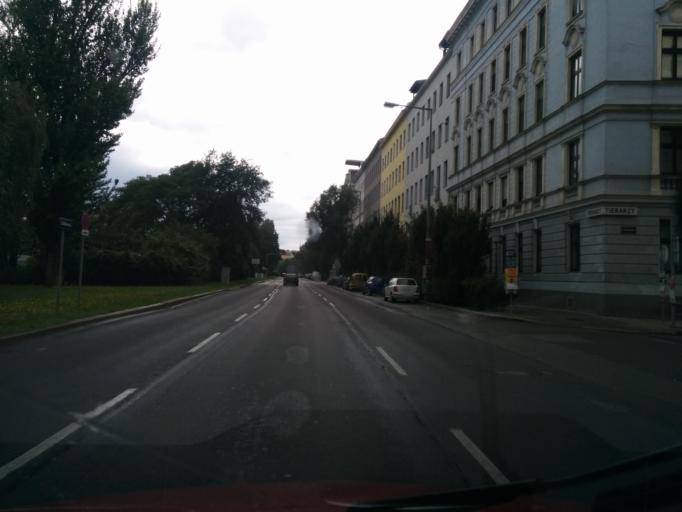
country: AT
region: Vienna
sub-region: Wien Stadt
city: Vienna
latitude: 48.2026
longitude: 16.4042
